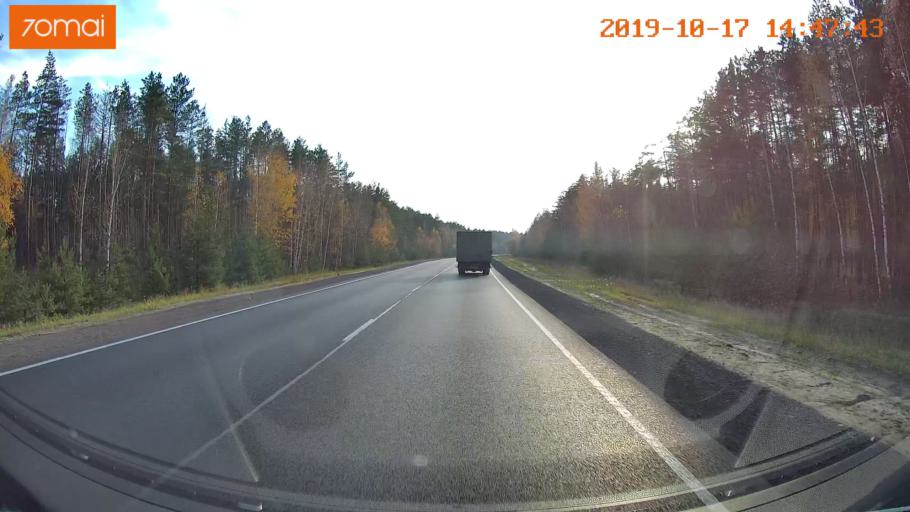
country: RU
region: Rjazan
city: Solotcha
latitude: 54.7676
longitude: 39.8580
